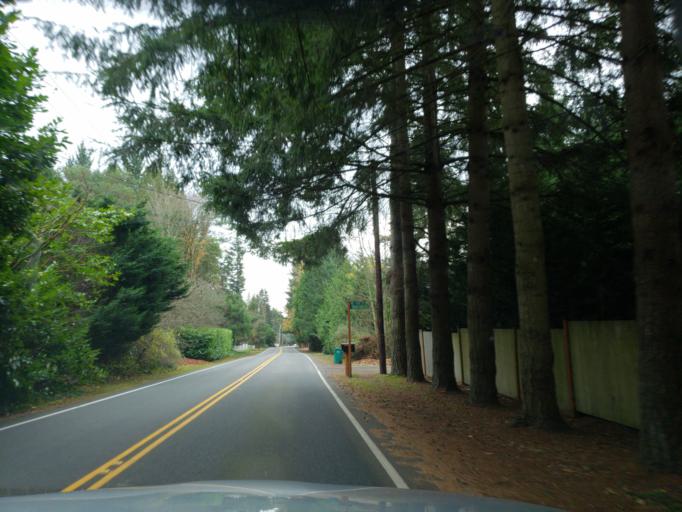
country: US
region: Washington
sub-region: King County
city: Woodinville
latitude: 47.7431
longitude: -122.1286
